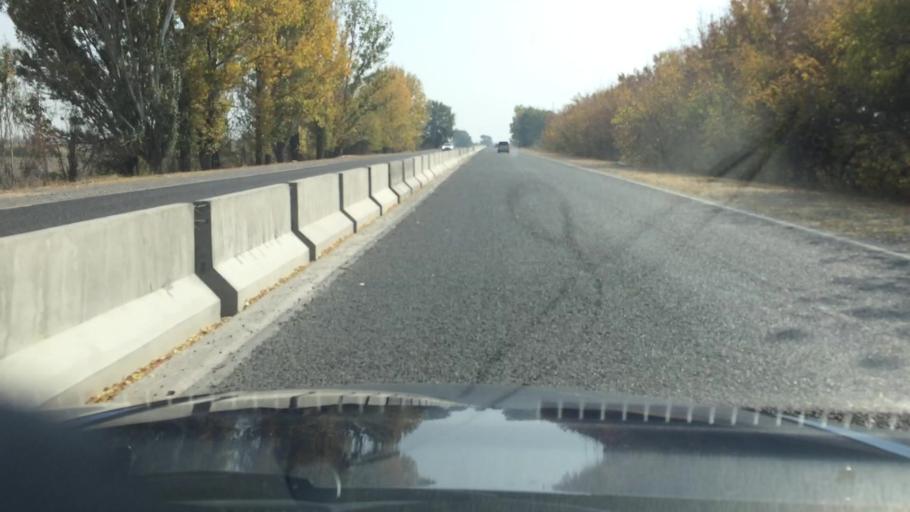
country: KG
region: Chuy
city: Kant
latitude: 42.9635
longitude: 74.9161
